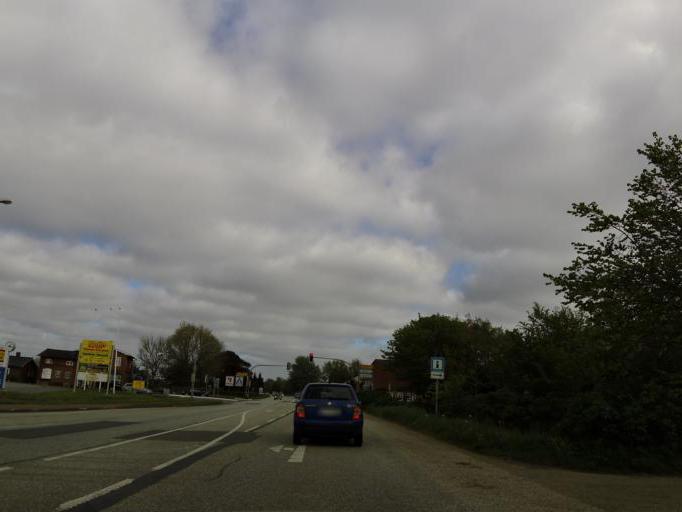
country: DE
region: Schleswig-Holstein
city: Risum-Lindholm
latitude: 54.7621
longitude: 8.8745
